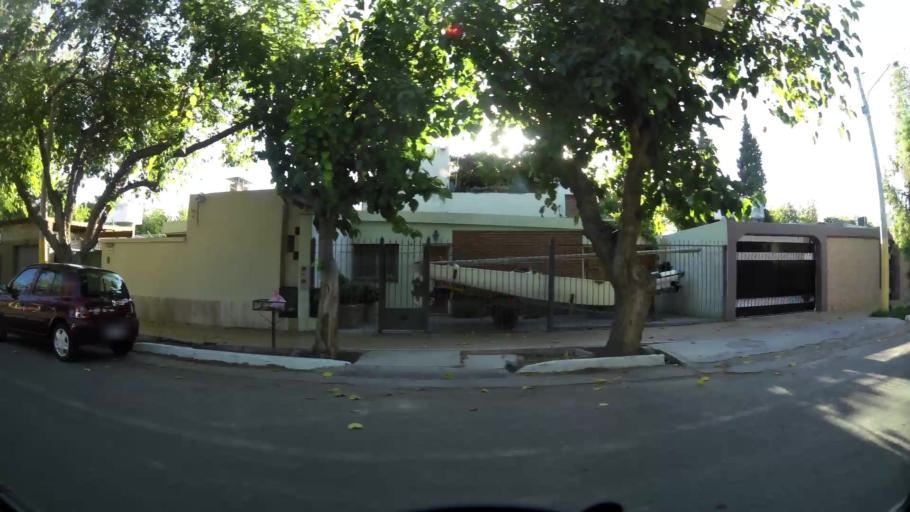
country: AR
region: San Juan
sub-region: Departamento de Santa Lucia
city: Santa Lucia
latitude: -31.5386
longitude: -68.5052
